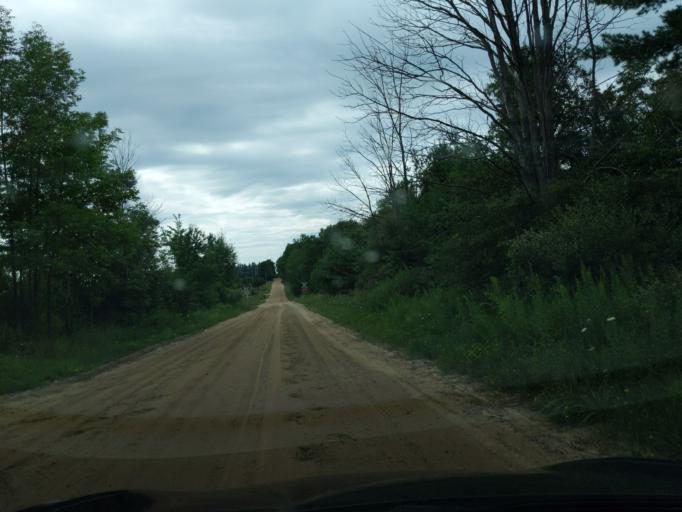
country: US
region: Michigan
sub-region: Clare County
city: Harrison
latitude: 44.0025
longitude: -84.9730
